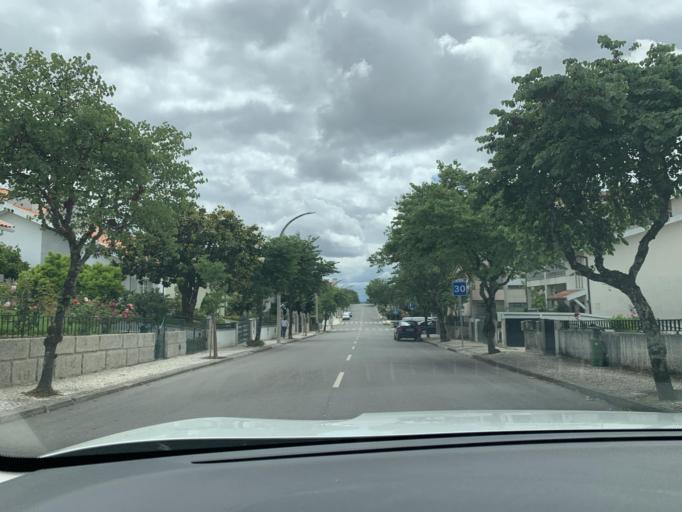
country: PT
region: Viseu
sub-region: Viseu
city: Rio de Loba
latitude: 40.6512
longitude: -7.8912
